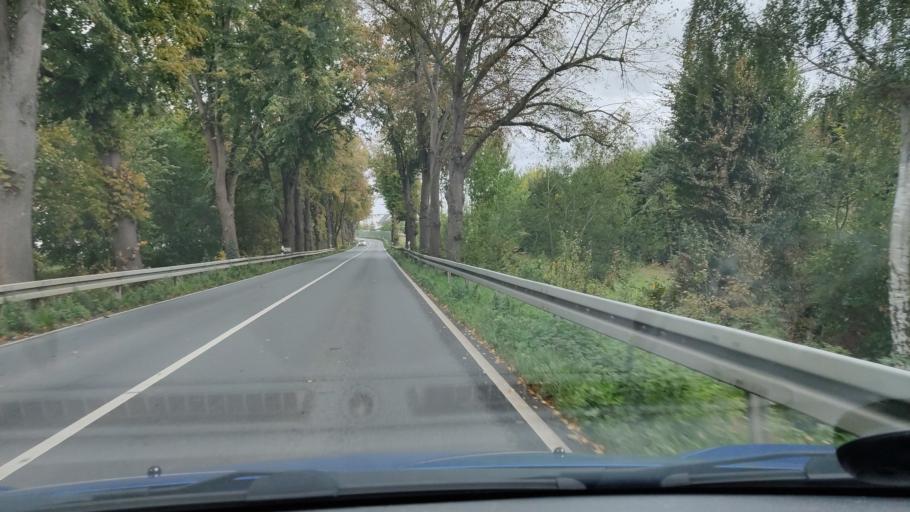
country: DE
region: Lower Saxony
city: Seelze
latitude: 52.3899
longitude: 9.5855
